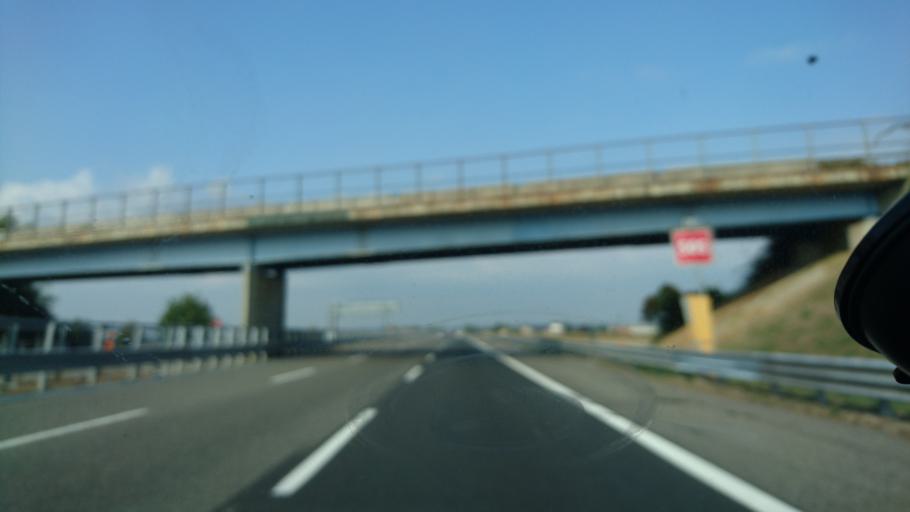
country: IT
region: Piedmont
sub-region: Provincia di Alessandria
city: Castellazzo Bormida
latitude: 44.8873
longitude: 8.5693
